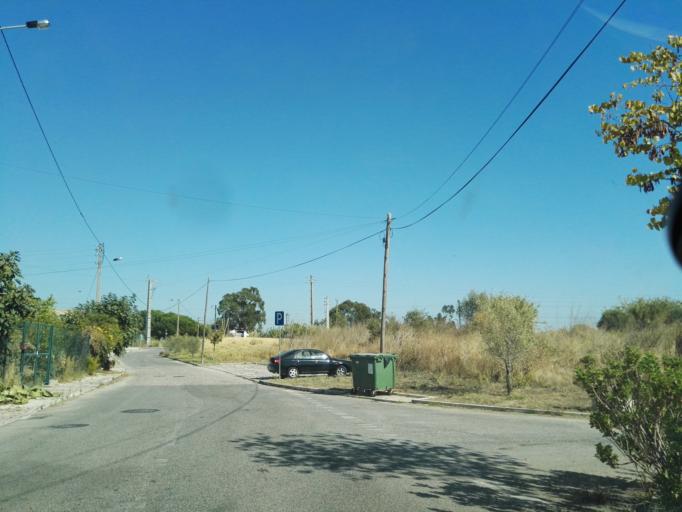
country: PT
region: Lisbon
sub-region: Vila Franca de Xira
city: Sobralinho
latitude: 38.9020
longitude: -9.0243
